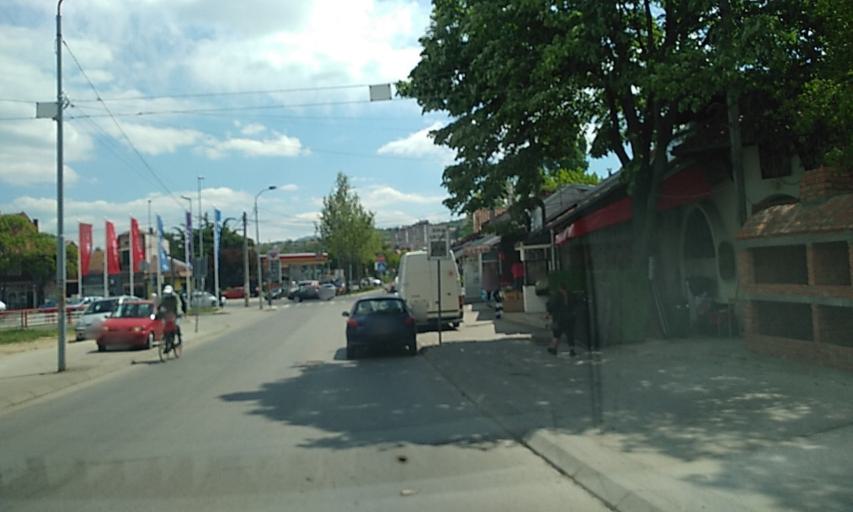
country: RS
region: Central Serbia
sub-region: Nisavski Okrug
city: Nis
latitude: 43.3168
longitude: 21.8832
